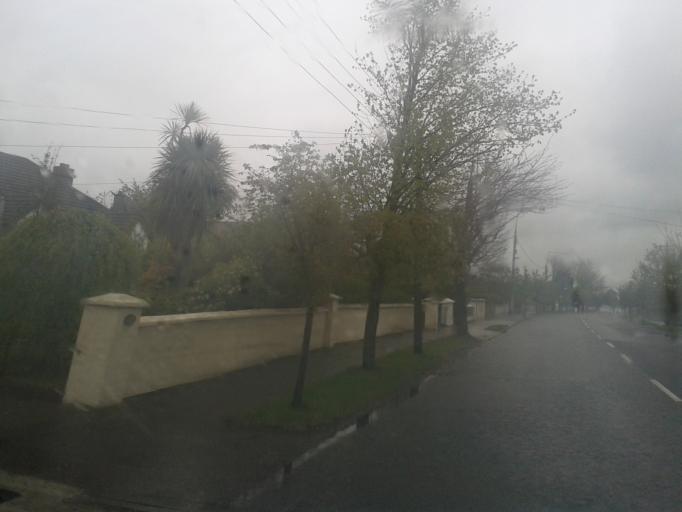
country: IE
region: Leinster
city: Templeogue
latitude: 53.3084
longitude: -6.3169
